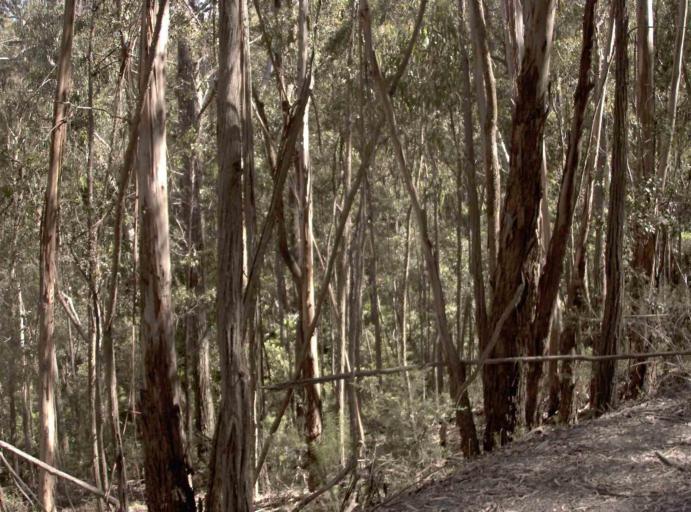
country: AU
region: New South Wales
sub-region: Bombala
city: Bombala
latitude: -37.2626
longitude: 148.7290
